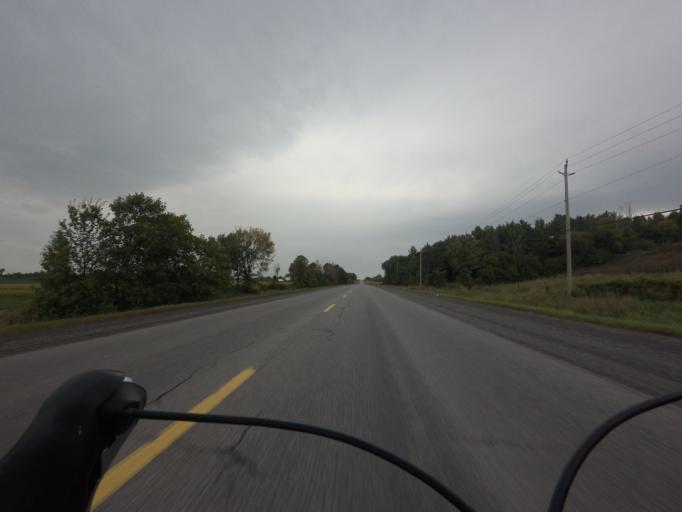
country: CA
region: Ontario
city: Bells Corners
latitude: 45.1615
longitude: -75.7095
